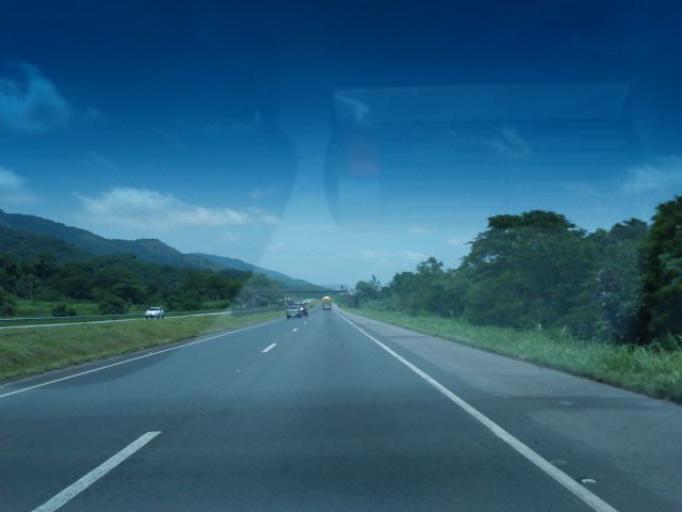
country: BR
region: Sao Paulo
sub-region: Miracatu
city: Miracatu
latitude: -24.2750
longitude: -47.4123
